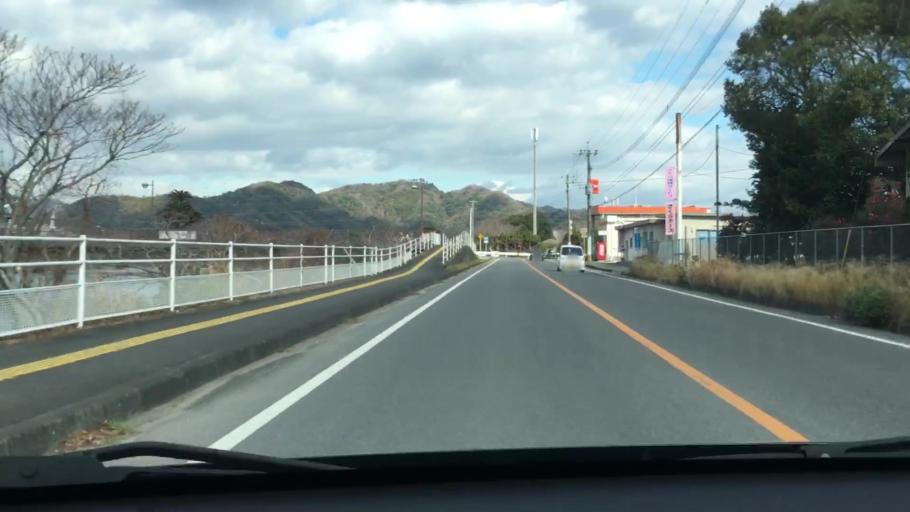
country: JP
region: Oita
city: Saiki
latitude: 32.9674
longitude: 131.9153
